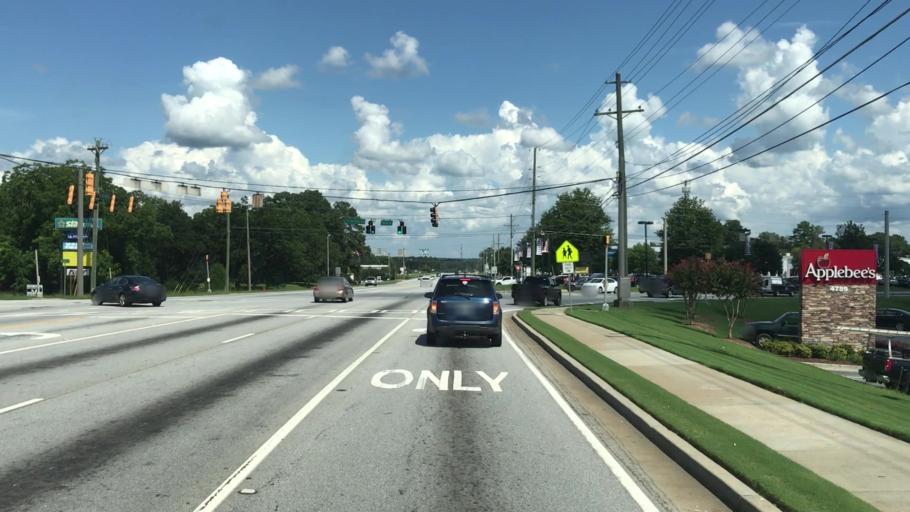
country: US
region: Georgia
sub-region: Walton County
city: Loganville
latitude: 33.8328
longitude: -83.8823
